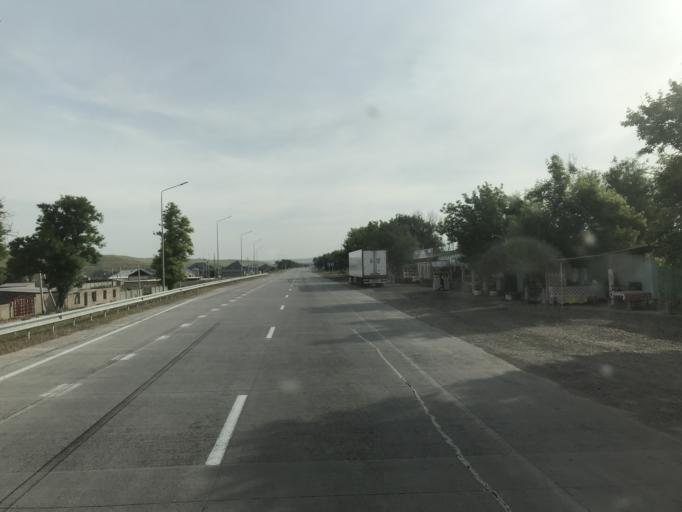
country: KZ
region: Ongtustik Qazaqstan
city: Qazyqurt
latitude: 41.9045
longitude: 69.4639
